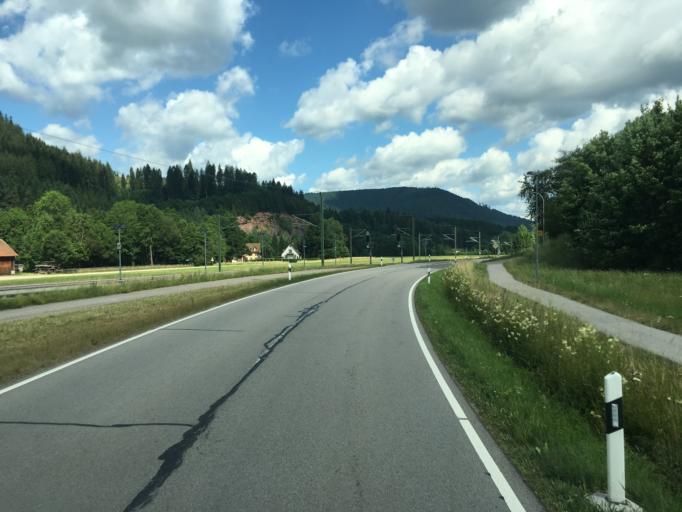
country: DE
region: Baden-Wuerttemberg
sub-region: Karlsruhe Region
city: Baiersbronn
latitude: 48.5365
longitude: 8.3997
